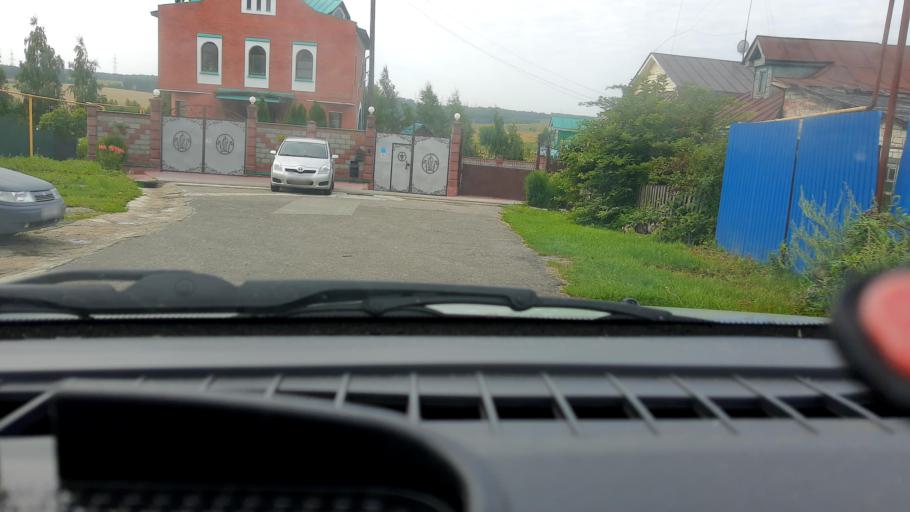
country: RU
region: Nizjnij Novgorod
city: Nizhniy Novgorod
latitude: 56.2322
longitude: 43.9964
